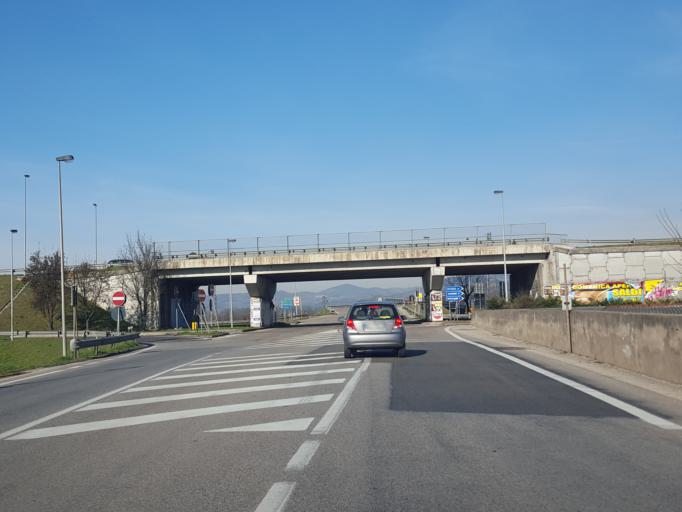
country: IT
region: Veneto
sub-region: Provincia di Vicenza
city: Monticello di Fara
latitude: 45.4355
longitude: 11.3628
